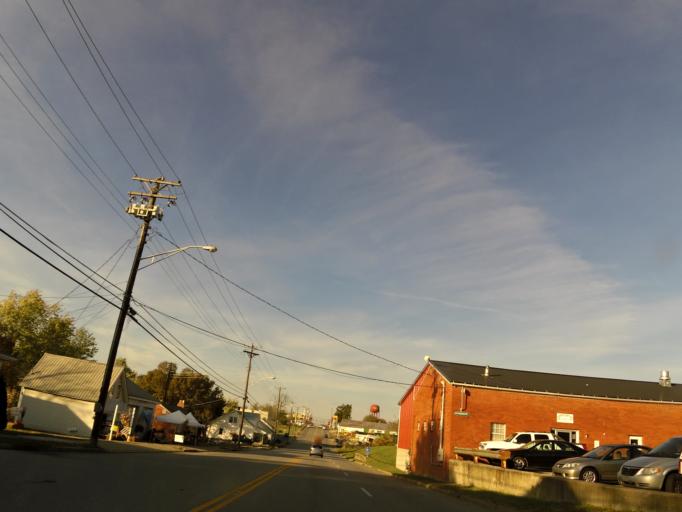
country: US
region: Kentucky
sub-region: Garrard County
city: Lancaster
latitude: 37.6126
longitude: -84.5798
